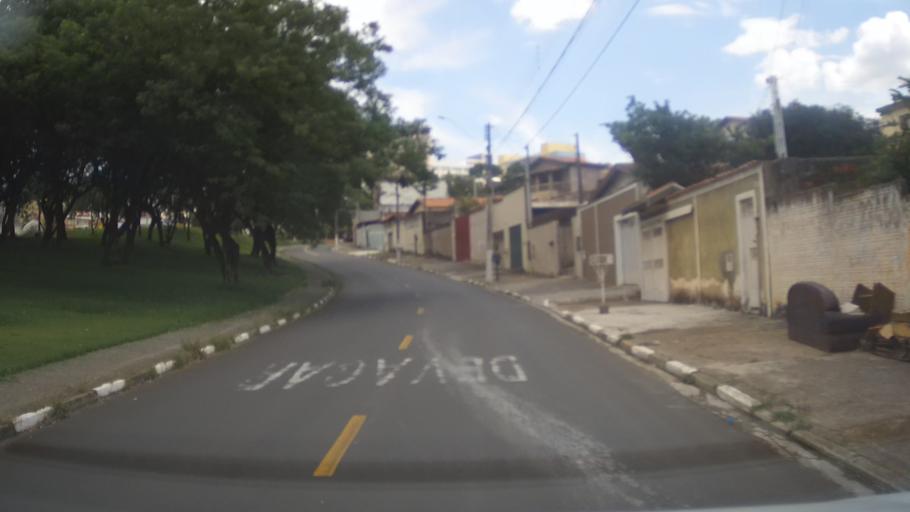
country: BR
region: Sao Paulo
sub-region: Campinas
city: Campinas
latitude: -22.9209
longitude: -47.0374
